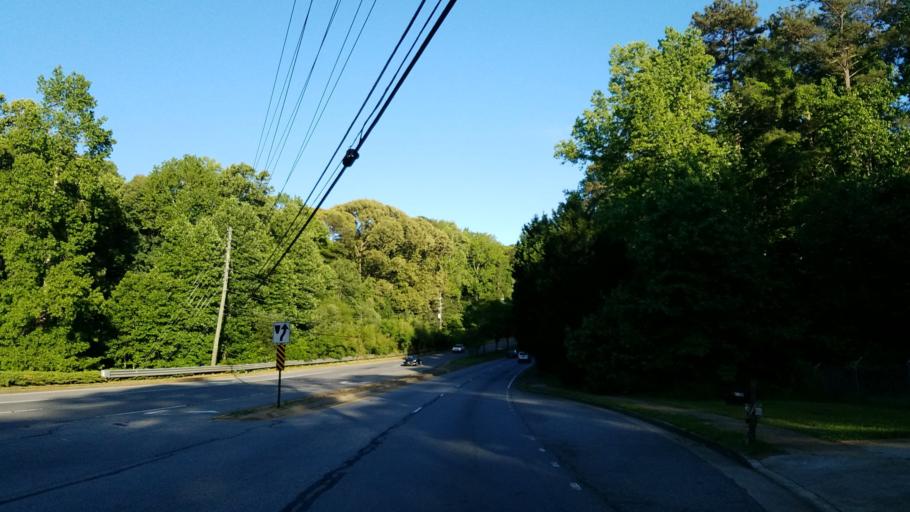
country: US
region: Georgia
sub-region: Cherokee County
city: Woodstock
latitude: 34.0654
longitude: -84.5628
